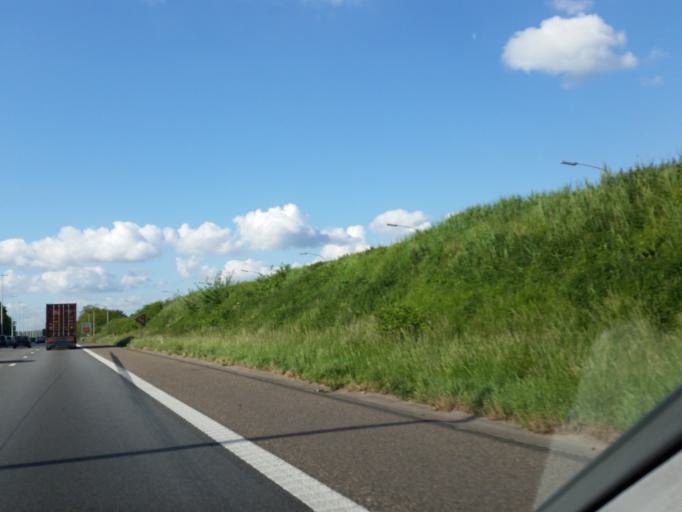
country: BE
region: Flanders
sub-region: Provincie Antwerpen
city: Kontich
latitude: 51.1236
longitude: 4.4304
